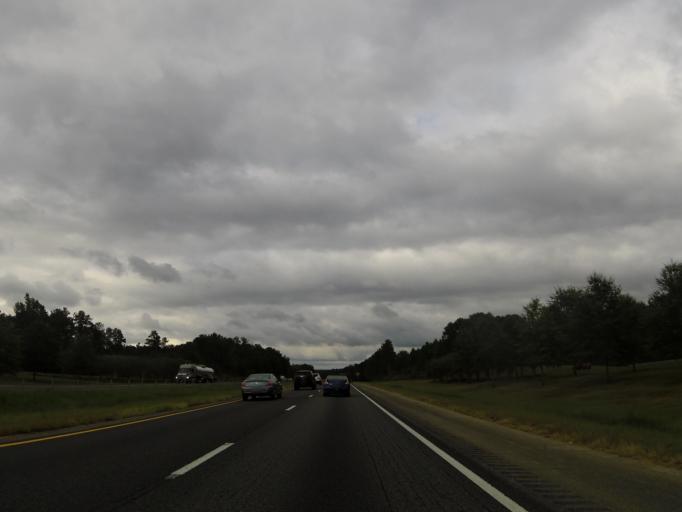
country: US
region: Alabama
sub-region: Butler County
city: Georgiana
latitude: 31.6512
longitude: -86.7747
